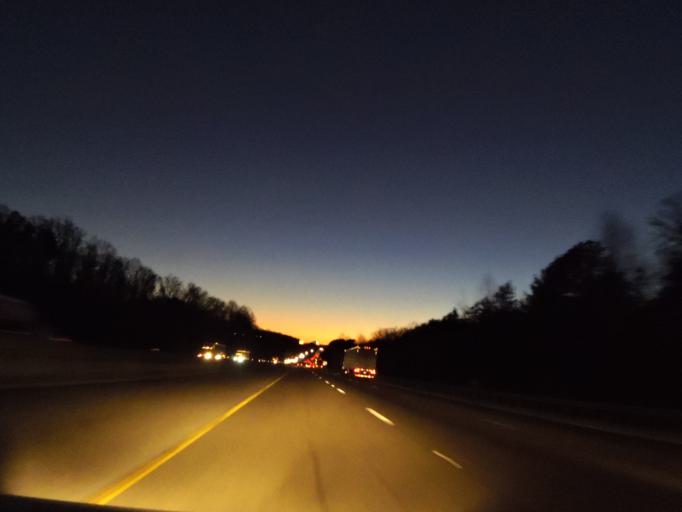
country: US
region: Tennessee
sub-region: Jefferson County
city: Dandridge
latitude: 36.0521
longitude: -83.4135
